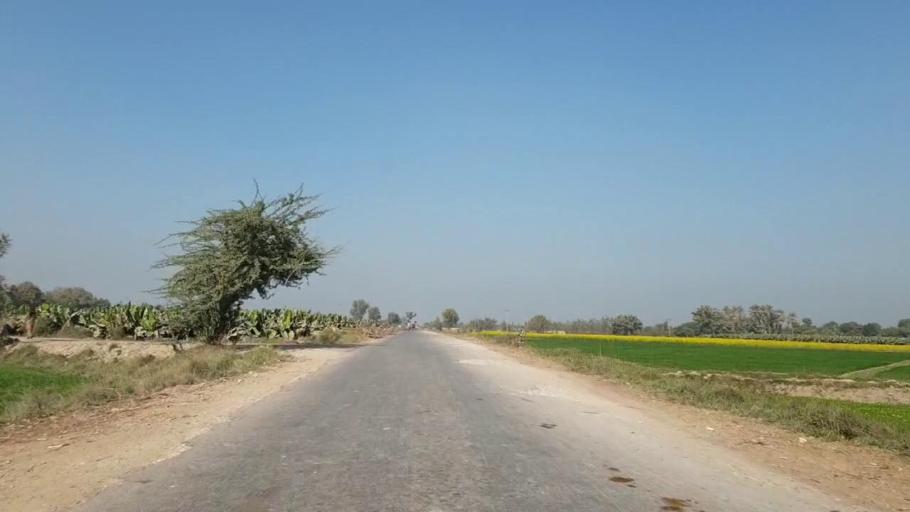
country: PK
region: Sindh
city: Tando Adam
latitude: 25.6437
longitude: 68.5937
